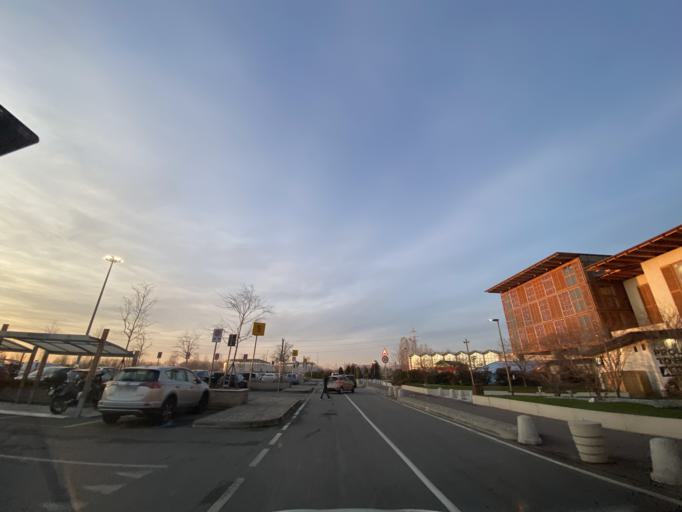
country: IT
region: Lombardy
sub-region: Citta metropolitana di Milano
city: Passirana
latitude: 45.5634
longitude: 9.0496
